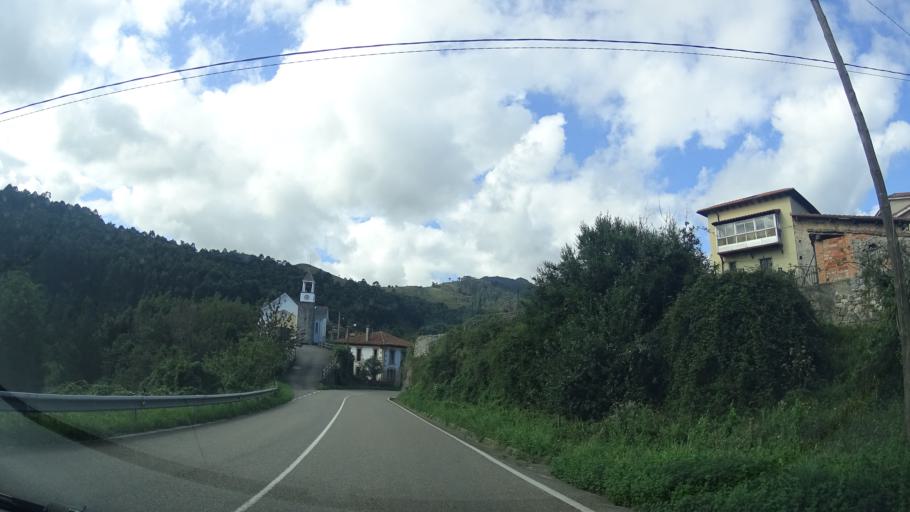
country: ES
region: Asturias
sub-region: Province of Asturias
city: Ribadesella
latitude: 43.4744
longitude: -5.1513
